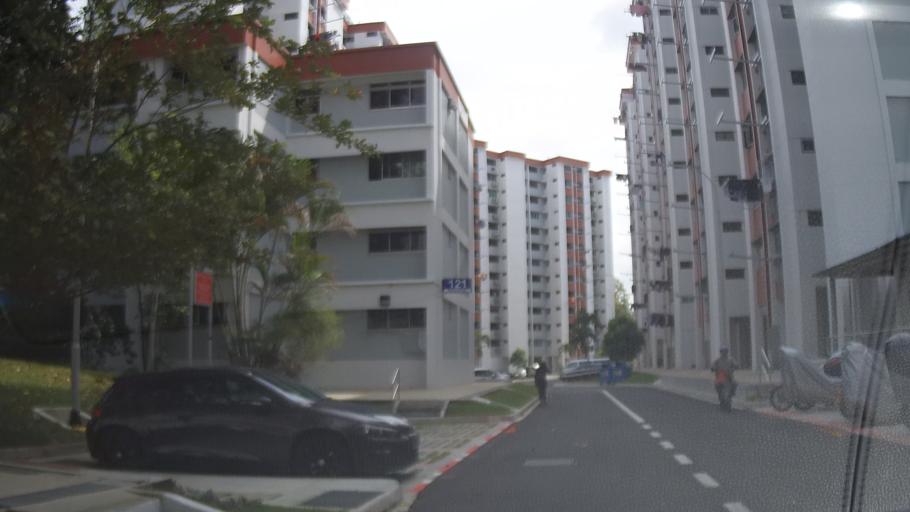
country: MY
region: Johor
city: Johor Bahru
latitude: 1.4389
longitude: 103.7797
